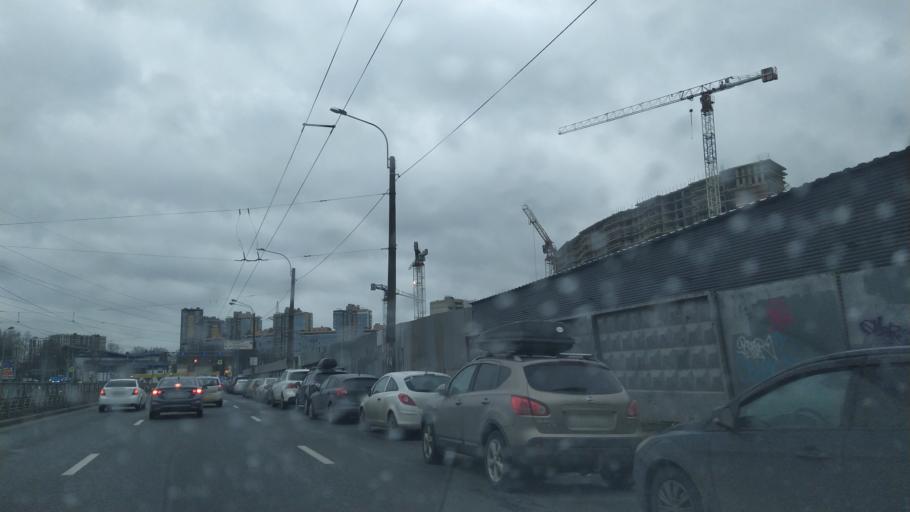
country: RU
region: Leningrad
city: Chernaya Rechka
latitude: 60.0021
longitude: 30.3043
